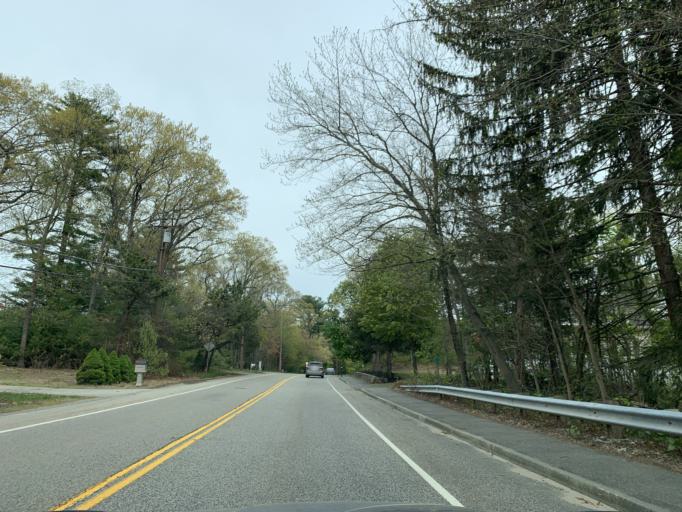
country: US
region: Massachusetts
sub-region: Norfolk County
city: Canton
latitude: 42.1371
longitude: -71.1541
